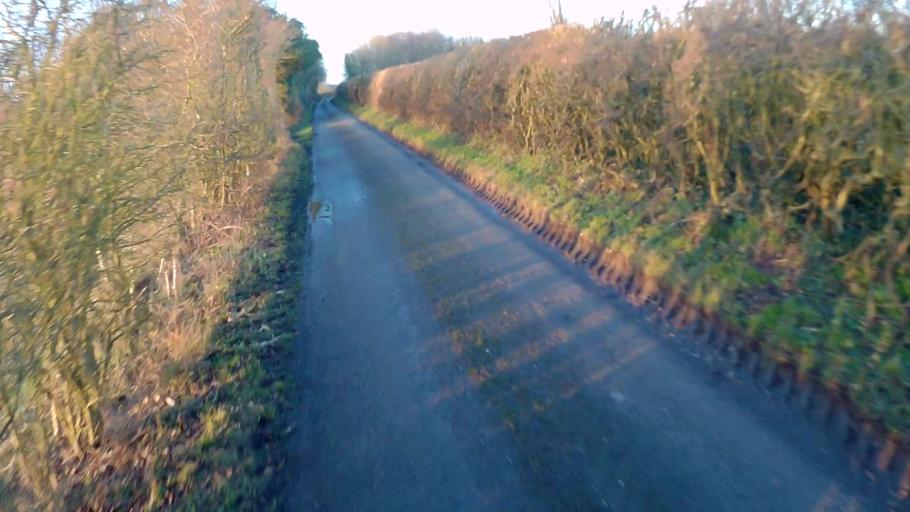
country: GB
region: England
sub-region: Hampshire
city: Overton
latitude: 51.2055
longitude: -1.2437
